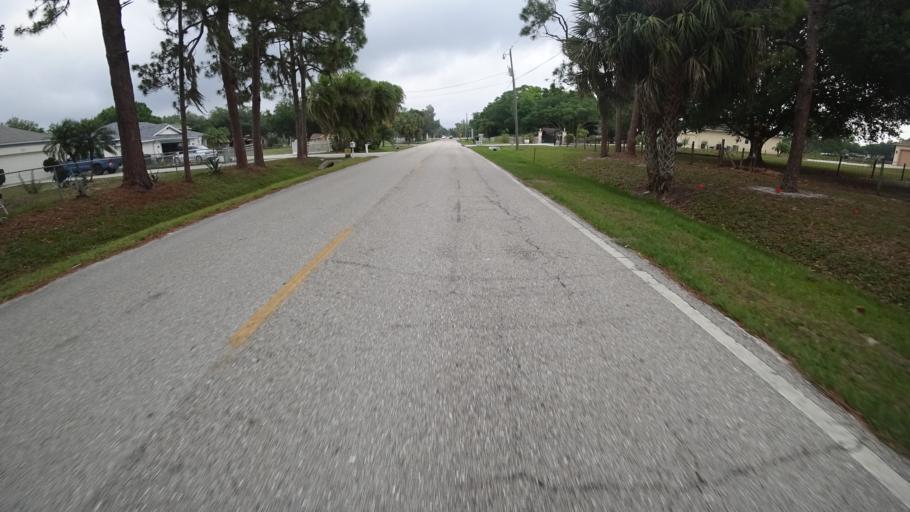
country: US
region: Florida
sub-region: Manatee County
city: Samoset
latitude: 27.4590
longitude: -82.5162
